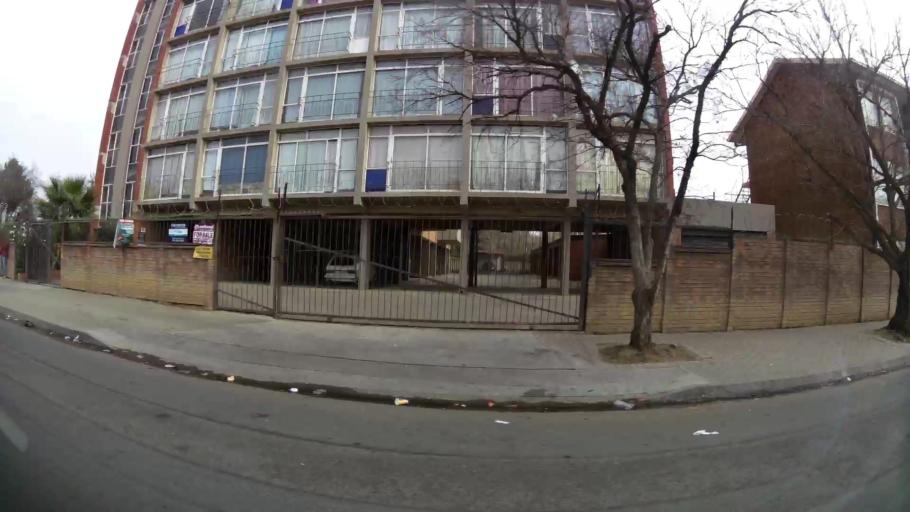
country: ZA
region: Orange Free State
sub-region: Mangaung Metropolitan Municipality
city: Bloemfontein
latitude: -29.1235
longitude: 26.2114
